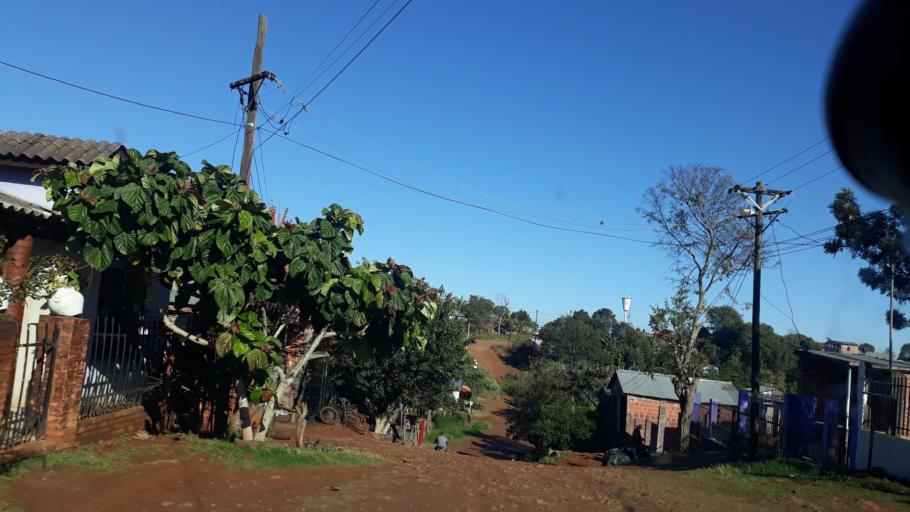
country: AR
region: Misiones
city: Bernardo de Irigoyen
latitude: -26.2618
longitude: -53.6543
